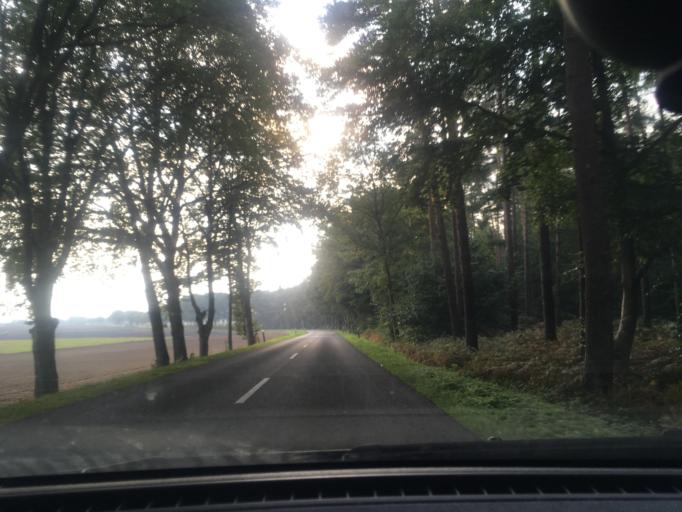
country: DE
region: Lower Saxony
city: Vastorf
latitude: 53.2152
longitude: 10.5562
